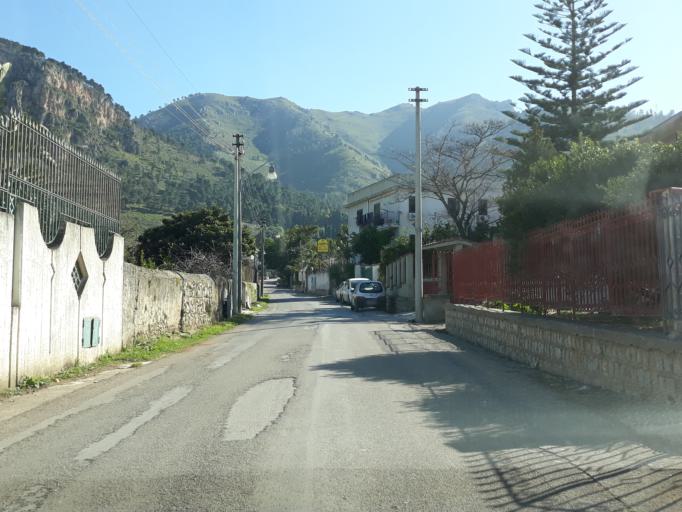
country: IT
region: Sicily
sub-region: Palermo
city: Villa Ciambra
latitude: 38.0789
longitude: 13.3468
